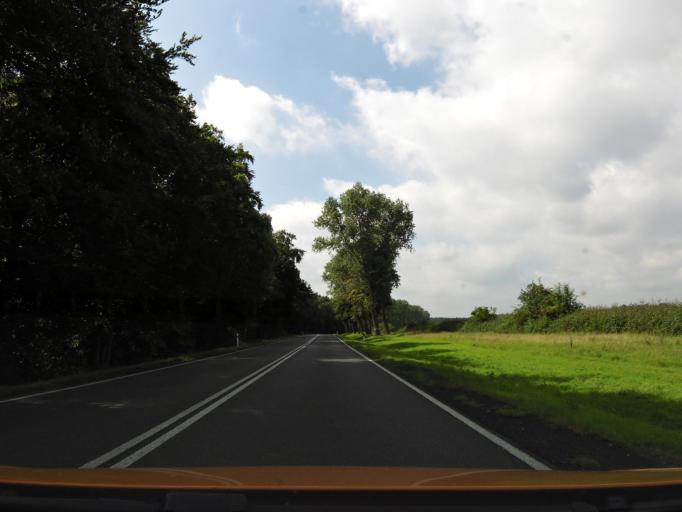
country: PL
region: West Pomeranian Voivodeship
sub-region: Powiat gryficki
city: Ploty
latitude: 53.8353
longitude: 15.3004
